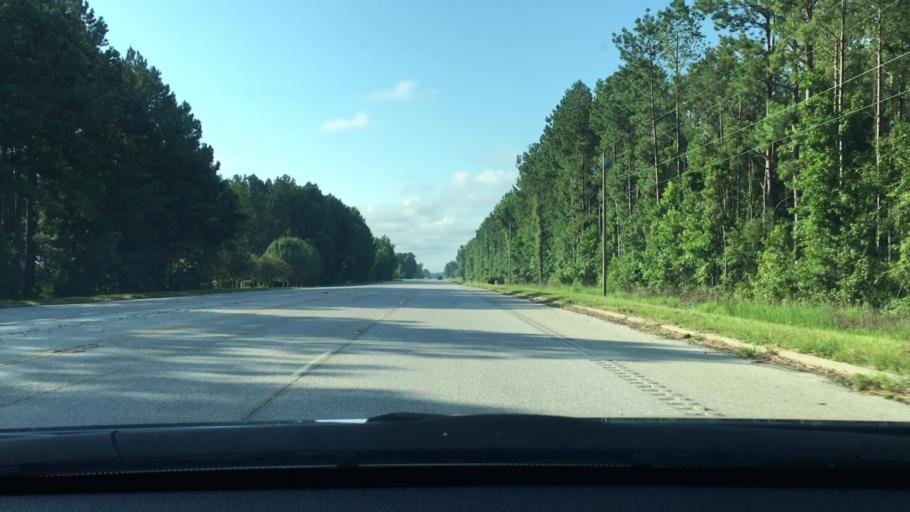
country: US
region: South Carolina
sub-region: Clarendon County
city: Manning
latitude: 33.7721
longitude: -80.2377
